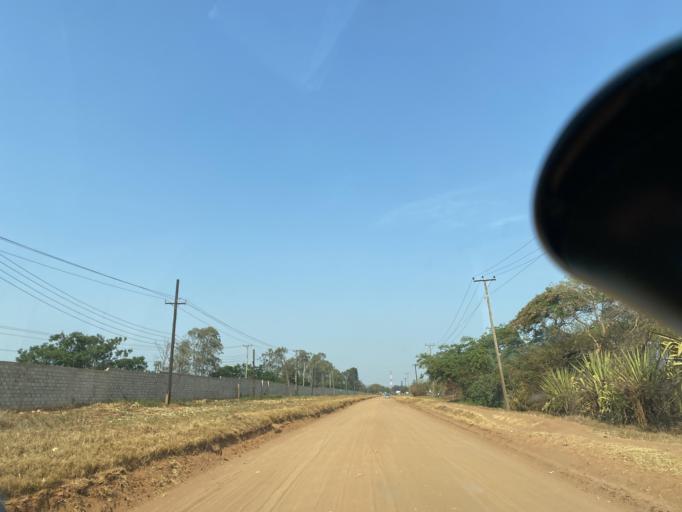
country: ZM
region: Lusaka
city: Lusaka
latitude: -15.4819
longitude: 28.1716
